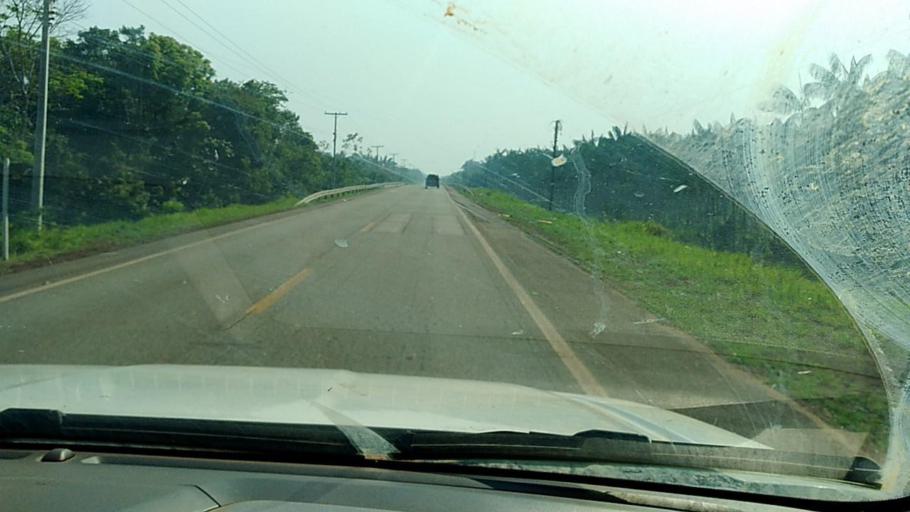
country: BR
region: Amazonas
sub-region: Humaita
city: Humaita
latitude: -7.8111
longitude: -63.1858
